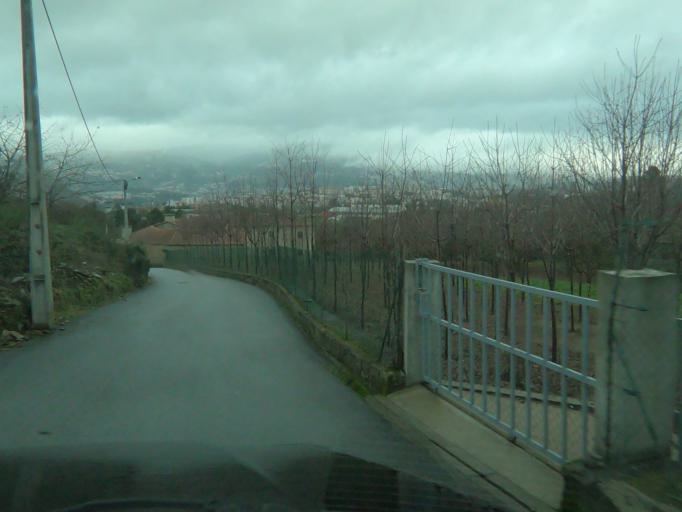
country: PT
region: Vila Real
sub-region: Vila Real
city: Vila Real
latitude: 41.2794
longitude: -7.7329
